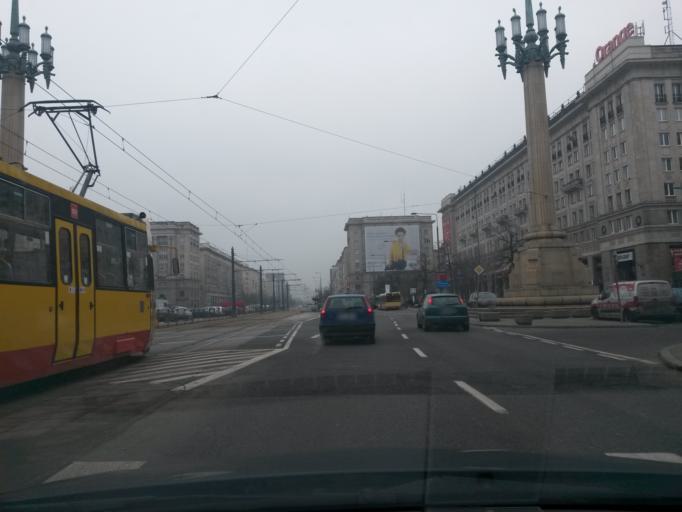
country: PL
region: Masovian Voivodeship
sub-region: Warszawa
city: Srodmiescie
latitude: 52.2216
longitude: 21.0167
